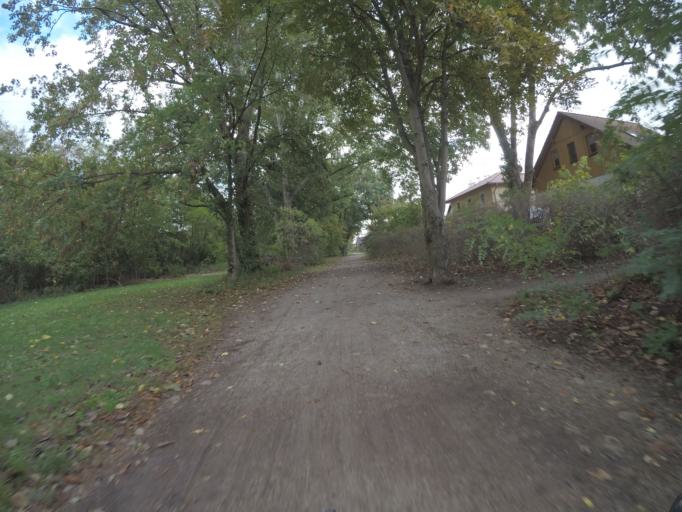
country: DE
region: Berlin
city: Alt-Hohenschoenhausen
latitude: 52.5639
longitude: 13.4889
